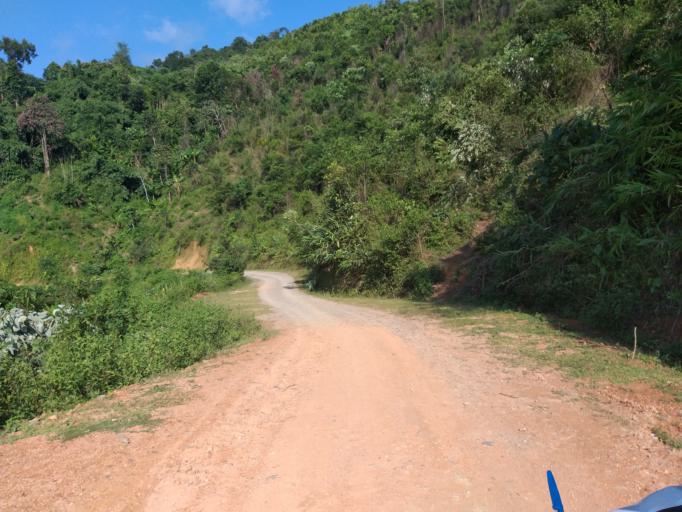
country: LA
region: Phongsali
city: Khoa
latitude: 21.1977
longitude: 102.6657
